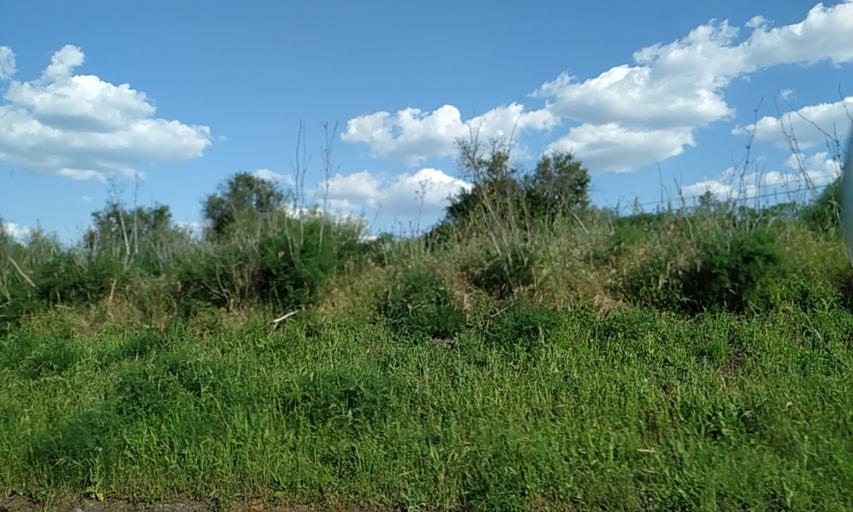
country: PT
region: Evora
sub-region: Estremoz
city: Estremoz
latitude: 38.8622
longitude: -7.5723
